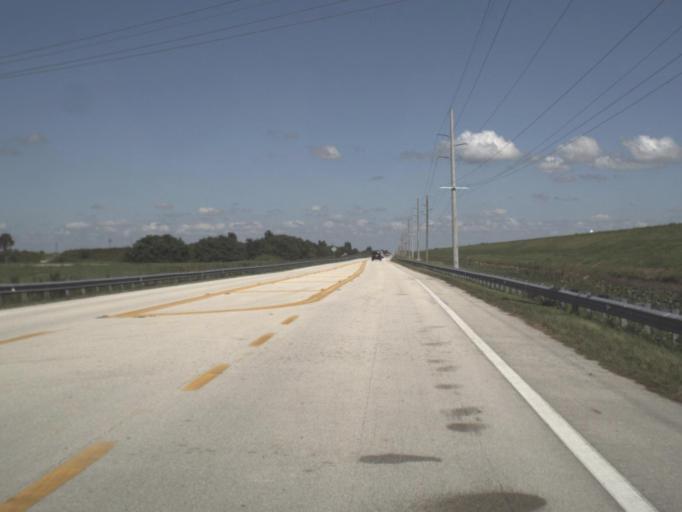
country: US
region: Florida
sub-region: Glades County
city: Moore Haven
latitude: 26.8902
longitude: -81.1225
